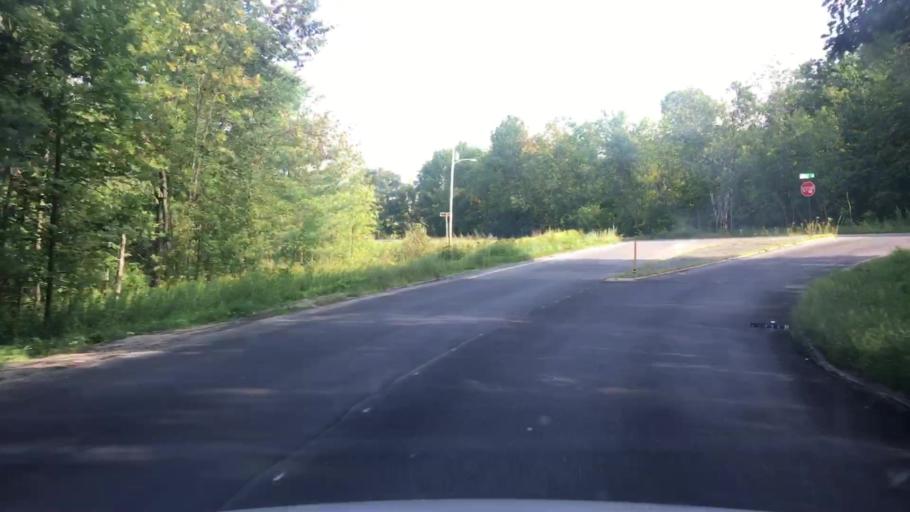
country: US
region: Maine
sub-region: Kennebec County
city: Waterville
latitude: 44.5677
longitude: -69.6525
